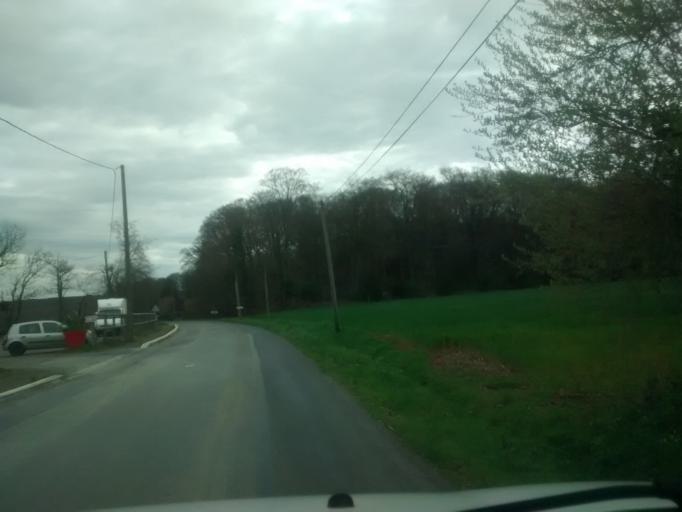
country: FR
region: Brittany
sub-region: Departement d'Ille-et-Vilaine
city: Betton
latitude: 48.1831
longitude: -1.6139
